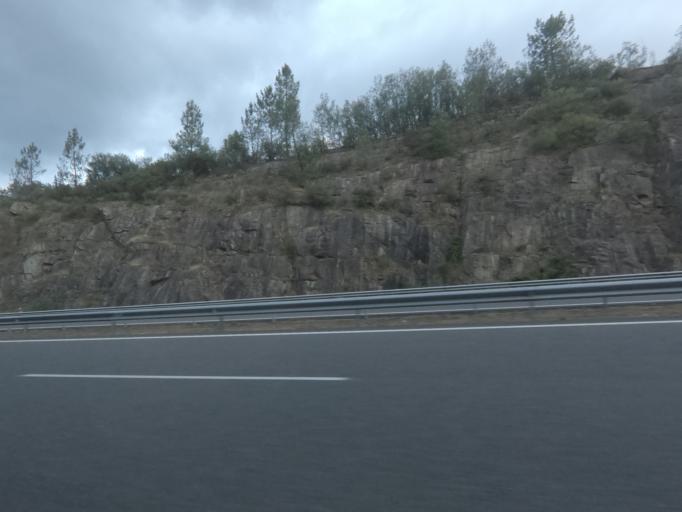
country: ES
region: Galicia
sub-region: Provincia de Ourense
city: Carballeda de Avia
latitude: 42.3063
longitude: -8.1548
